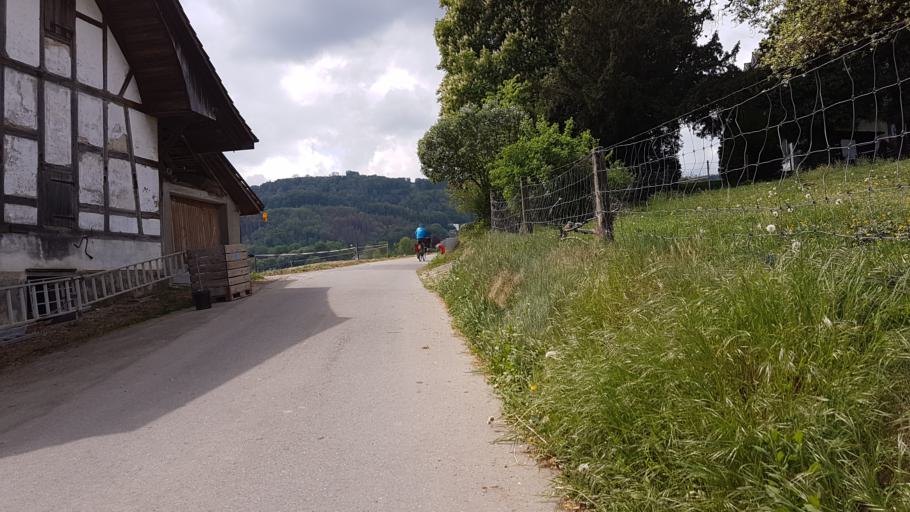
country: CH
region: Bern
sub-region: Bern-Mittelland District
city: Kehrsatz
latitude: 46.9174
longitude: 7.4771
